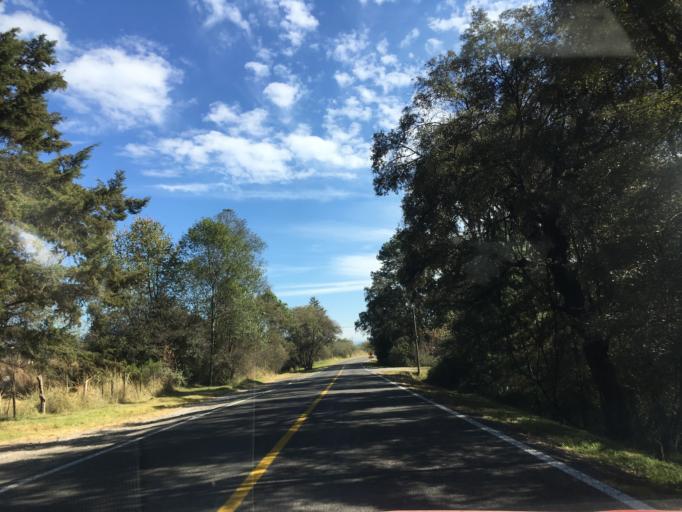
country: MX
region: Michoacan
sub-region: Hidalgo
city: Tierras Coloradas (San Pedro)
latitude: 19.6677
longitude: -100.7114
